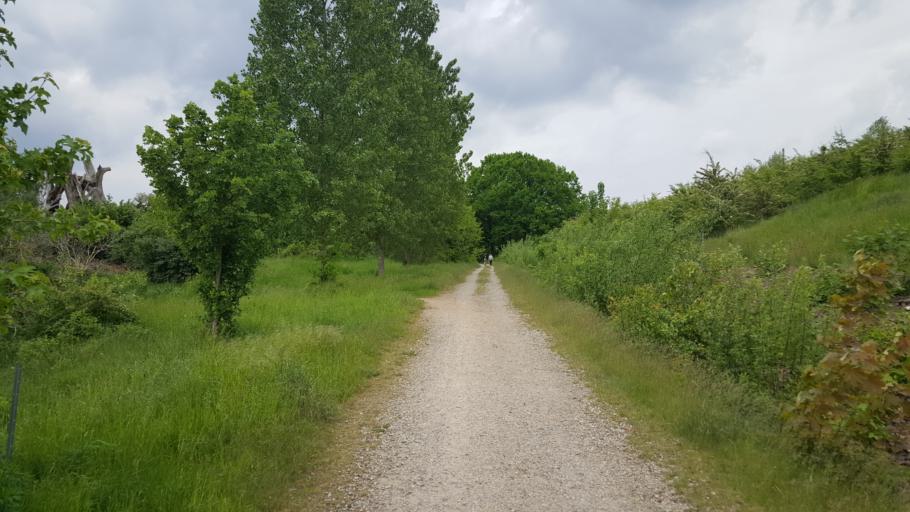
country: DE
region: Saxony
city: Albertstadt
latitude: 51.0847
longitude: 13.7522
